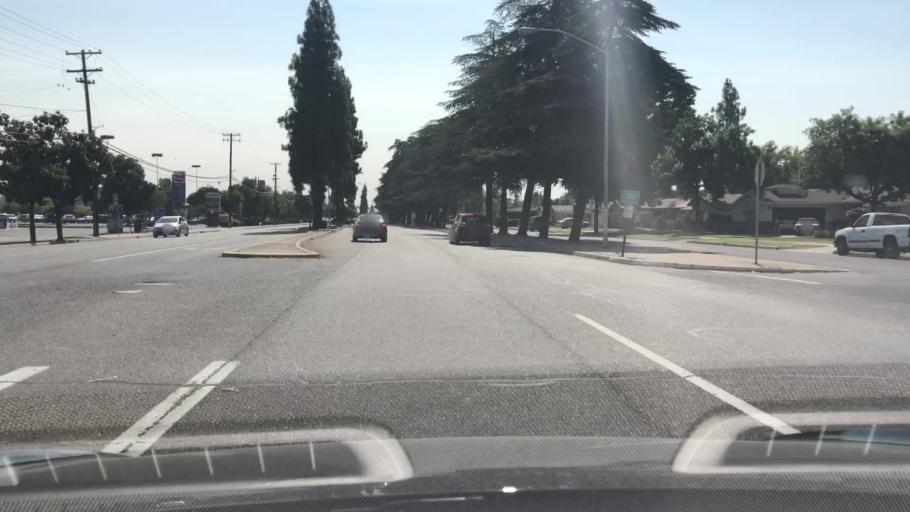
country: US
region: California
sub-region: Fresno County
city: Fresno
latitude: 36.7941
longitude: -119.7588
